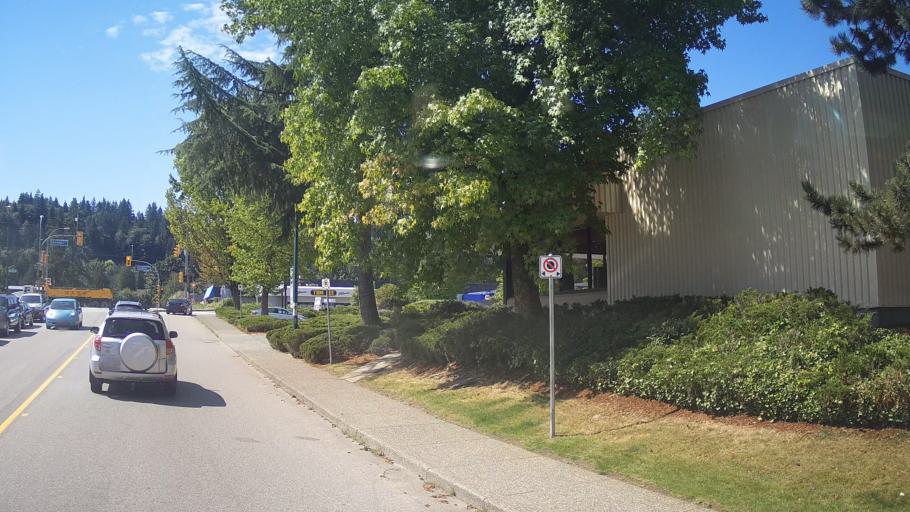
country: CA
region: British Columbia
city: Port Moody
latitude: 49.2788
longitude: -122.8183
